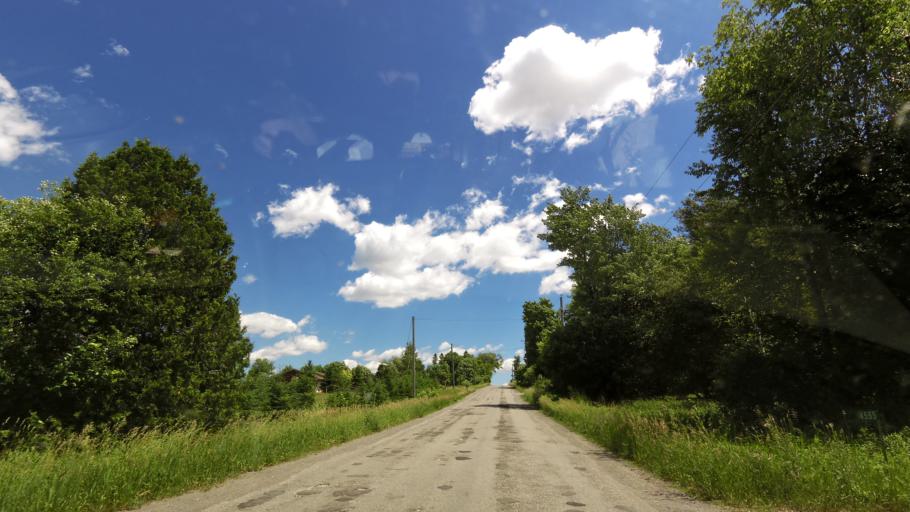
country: CA
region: Ontario
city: Omemee
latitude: 43.9754
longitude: -78.5027
